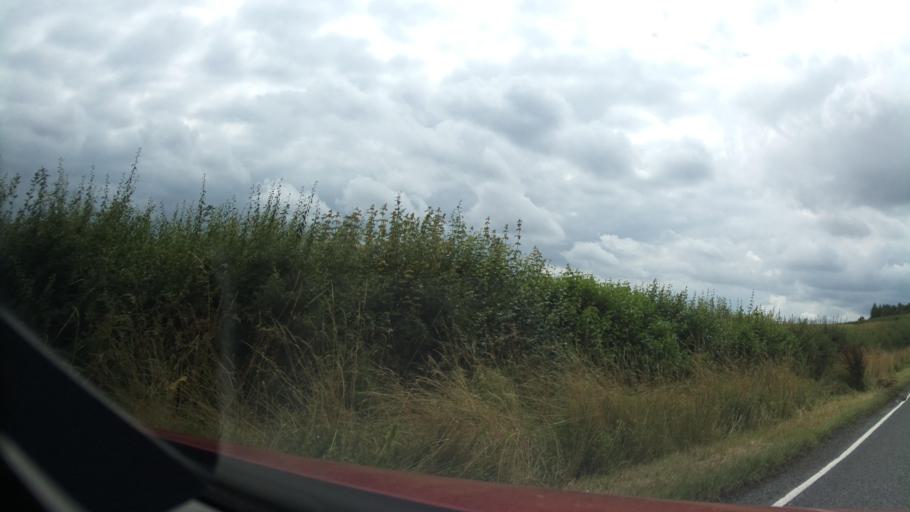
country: GB
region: England
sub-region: District of Rutland
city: Tickencote
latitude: 52.6810
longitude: -0.5062
